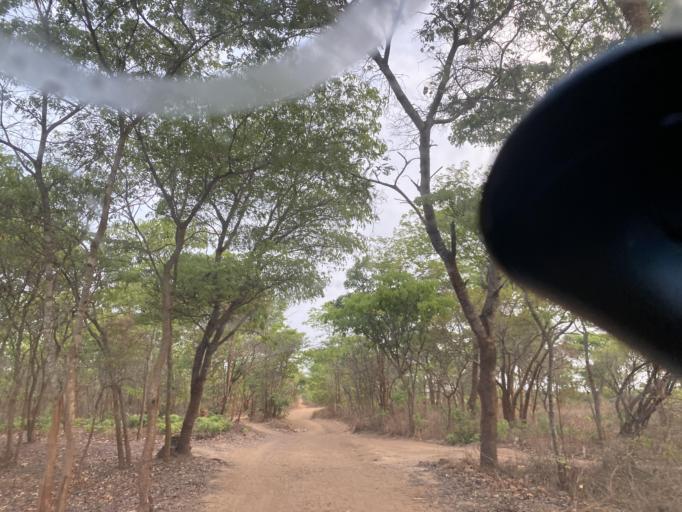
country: ZM
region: Lusaka
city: Chongwe
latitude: -15.1945
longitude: 28.4914
